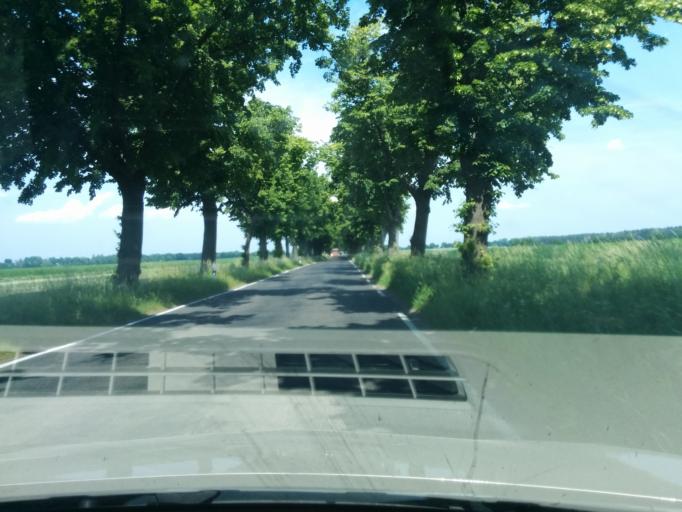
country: DE
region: Brandenburg
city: Bernau bei Berlin
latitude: 52.6330
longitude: 13.5746
